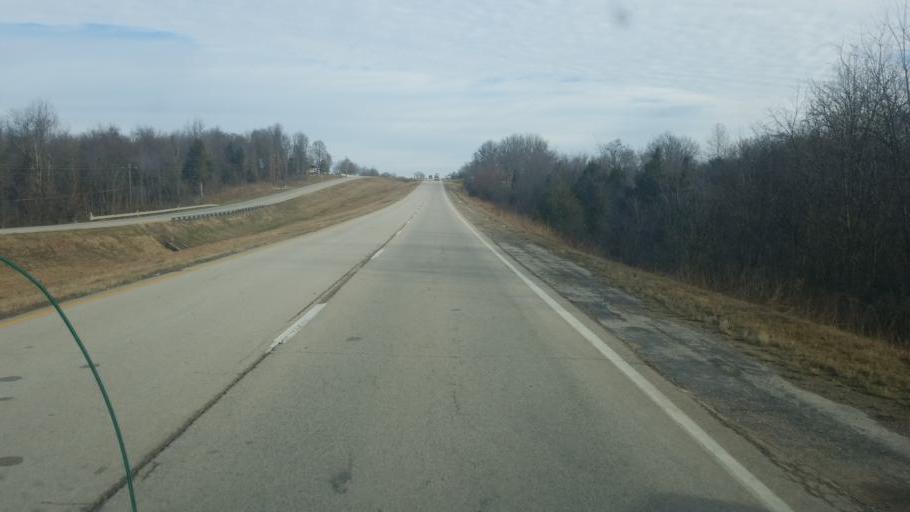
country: US
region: Missouri
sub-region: Stoddard County
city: Bloomfield
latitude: 36.8583
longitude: -89.9362
